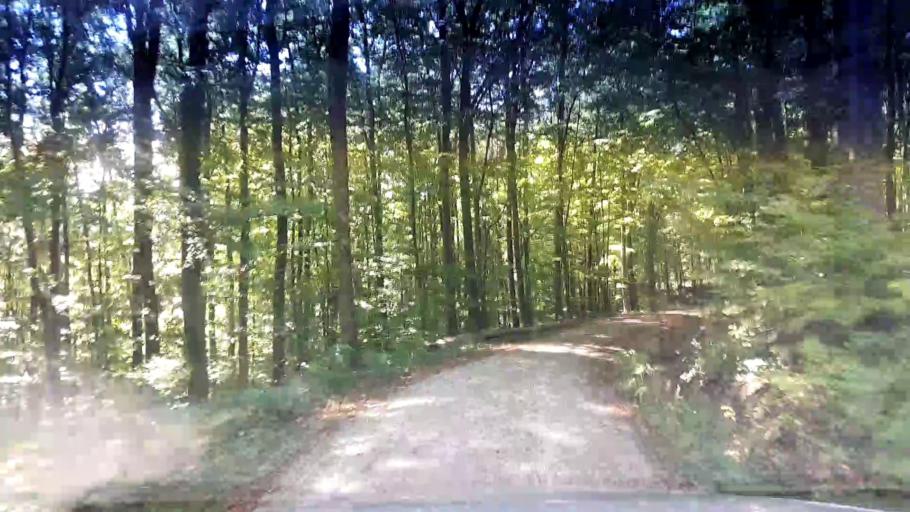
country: DE
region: Bavaria
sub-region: Upper Franconia
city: Litzendorf
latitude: 49.8821
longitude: 11.0401
